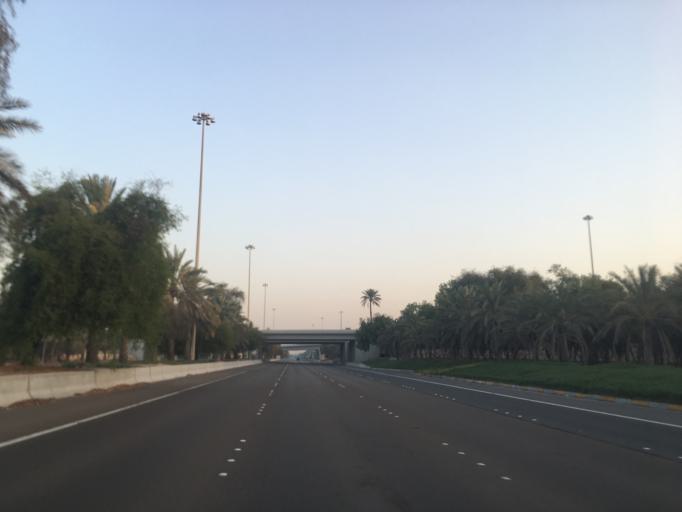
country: AE
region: Abu Dhabi
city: Abu Dhabi
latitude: 24.3893
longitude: 54.5398
